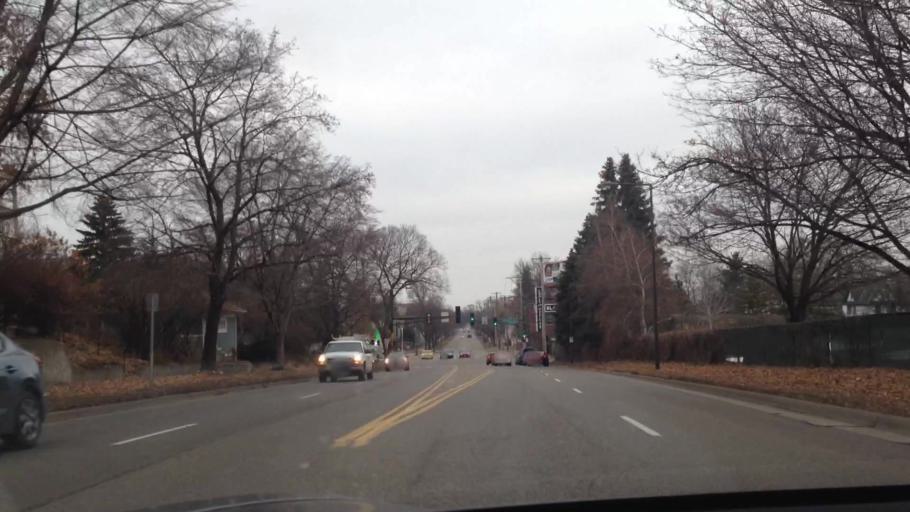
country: US
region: Minnesota
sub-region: Ramsey County
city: Falcon Heights
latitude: 44.9497
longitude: -93.1925
